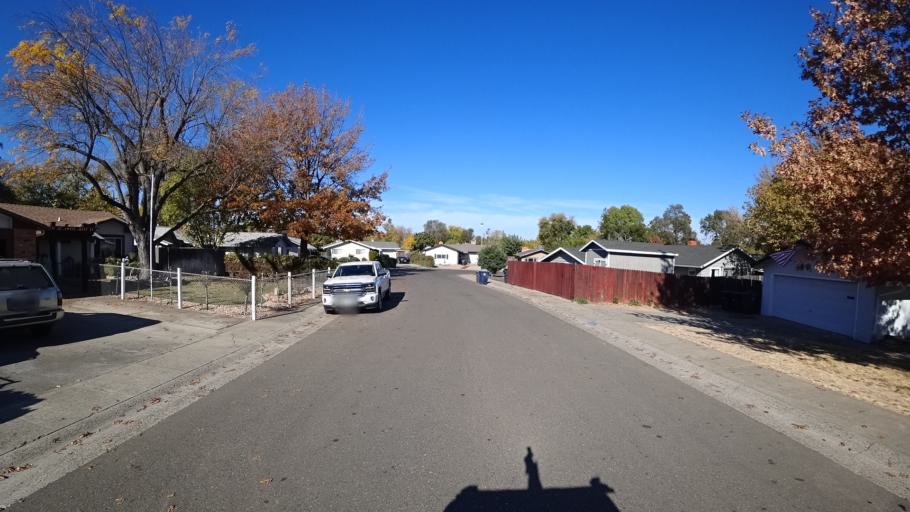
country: US
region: California
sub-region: Sacramento County
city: Antelope
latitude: 38.7145
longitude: -121.3066
